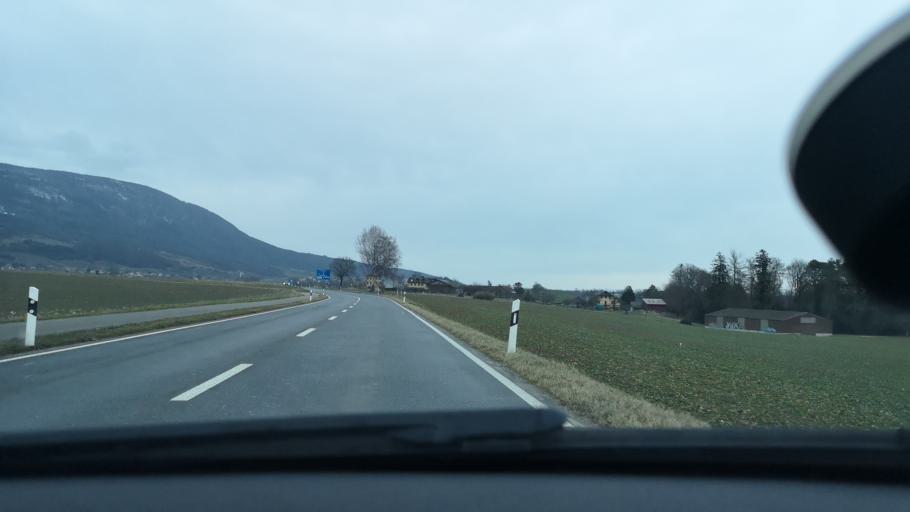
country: CH
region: Vaud
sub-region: Jura-Nord vaudois District
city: Grandson
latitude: 46.8175
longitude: 6.6562
